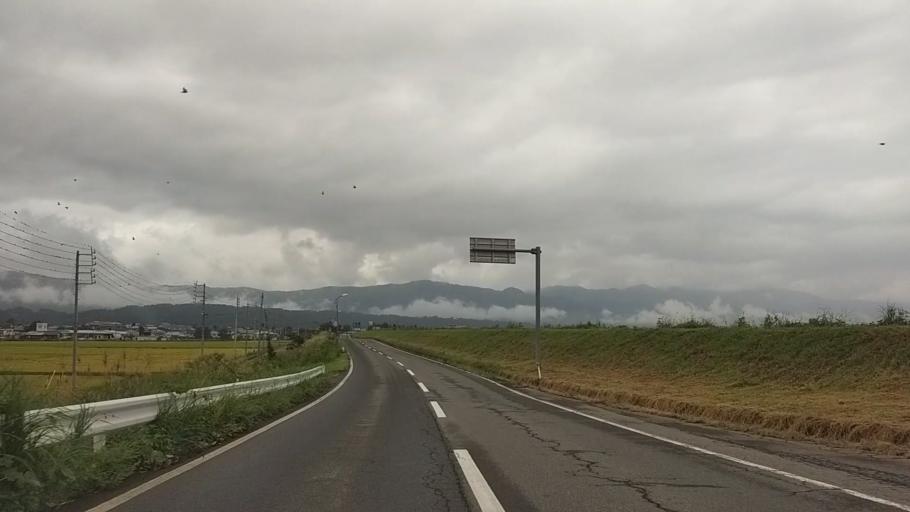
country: JP
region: Nagano
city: Iiyama
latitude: 36.8476
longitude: 138.3929
